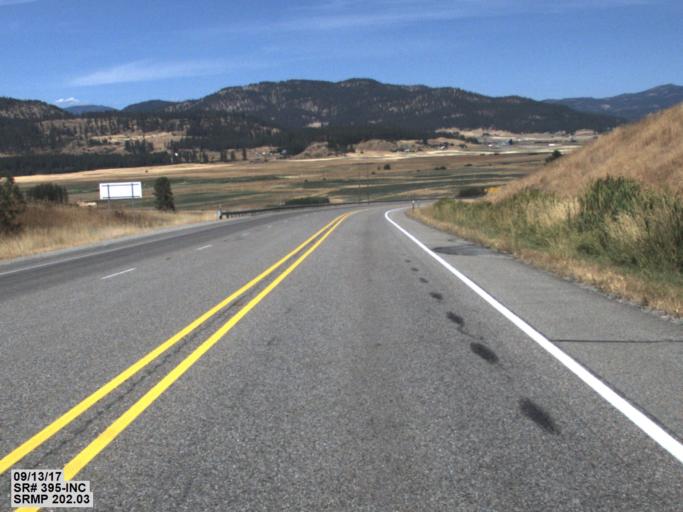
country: US
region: Washington
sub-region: Stevens County
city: Chewelah
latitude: 48.2027
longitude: -117.7126
